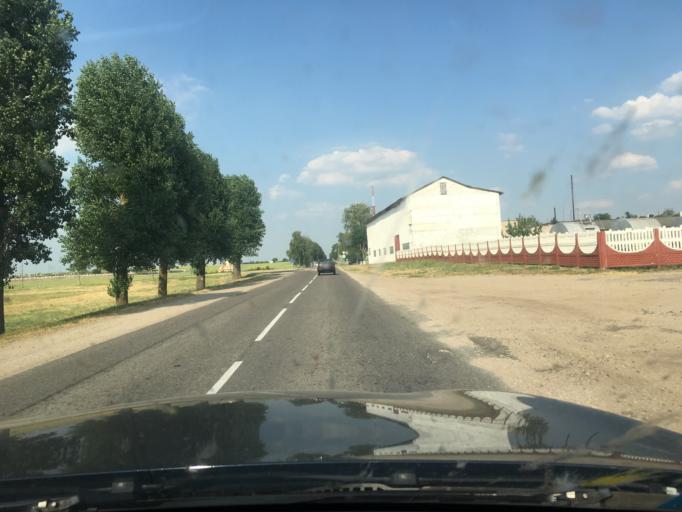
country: BY
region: Grodnenskaya
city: Svislach
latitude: 53.0415
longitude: 24.0833
